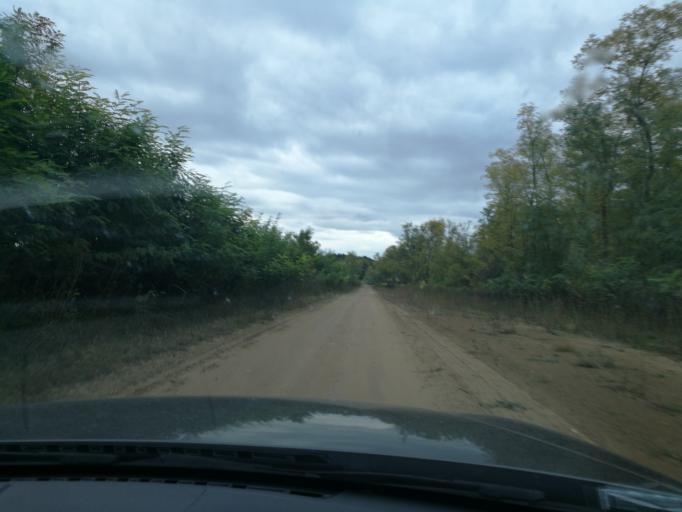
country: HU
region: Szabolcs-Szatmar-Bereg
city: Nyirpazony
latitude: 47.9930
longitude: 21.7883
